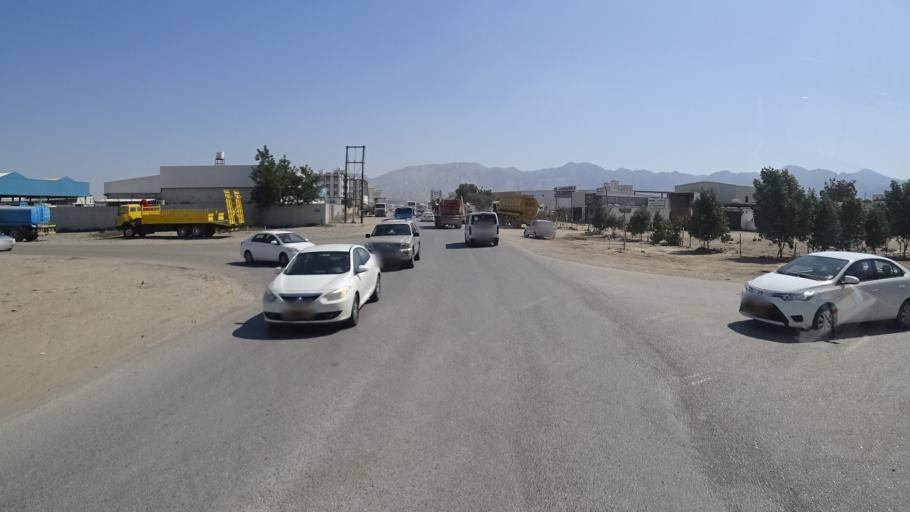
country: OM
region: Muhafazat Masqat
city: Bawshar
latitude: 23.5763
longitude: 58.3673
